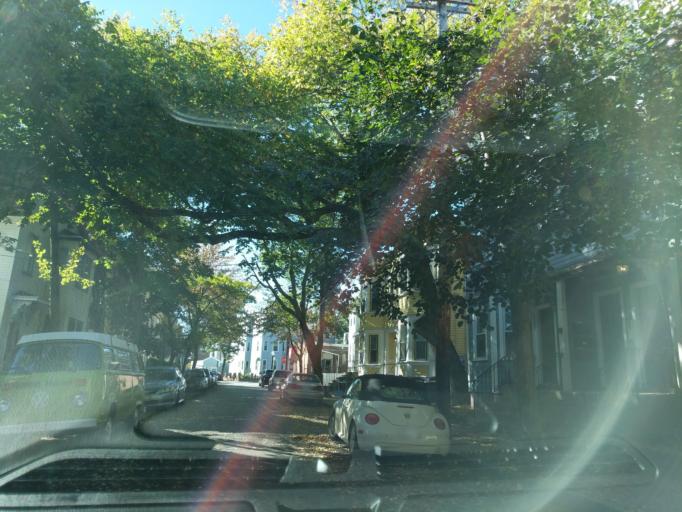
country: US
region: Massachusetts
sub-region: Middlesex County
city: Cambridge
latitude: 42.3652
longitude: -71.1129
